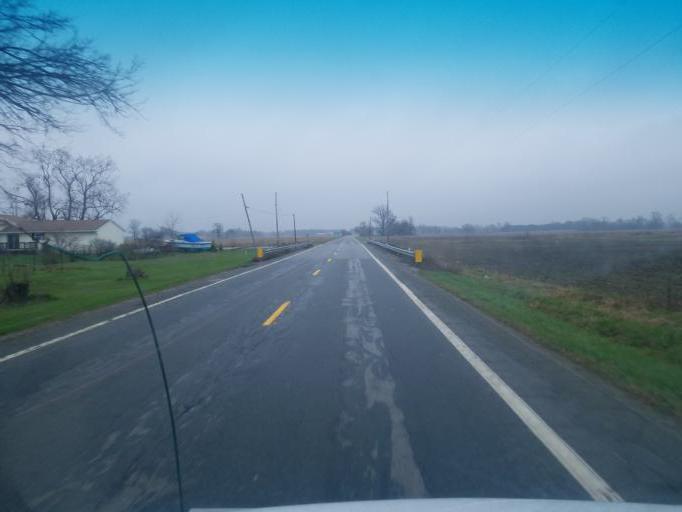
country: US
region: Ohio
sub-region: Wood County
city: Bowling Green
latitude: 41.3721
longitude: -83.7245
